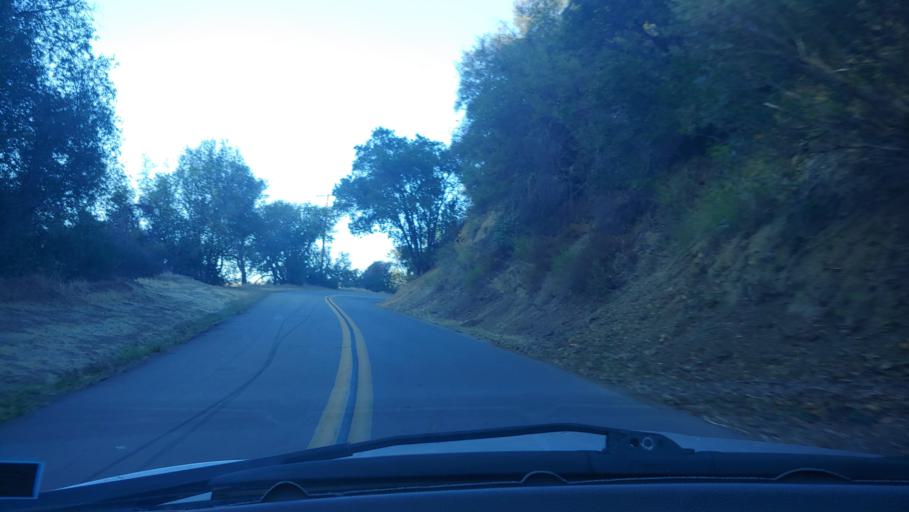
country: US
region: California
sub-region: Santa Barbara County
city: Goleta
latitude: 34.5216
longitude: -119.8379
